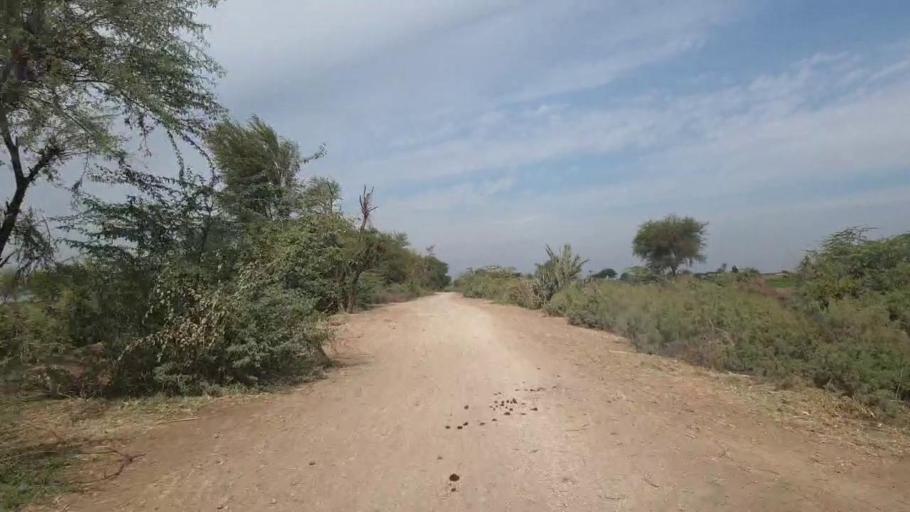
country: PK
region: Sindh
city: Sanghar
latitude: 26.0456
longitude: 68.9063
